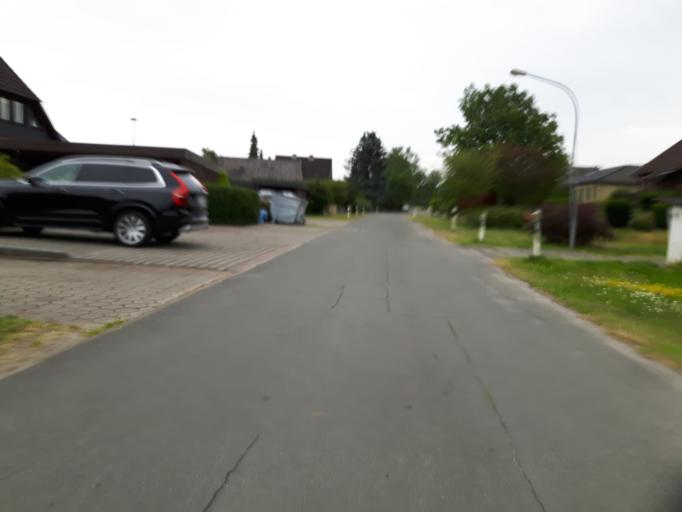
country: DE
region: Lower Saxony
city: Stelle
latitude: 53.4152
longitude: 10.0527
